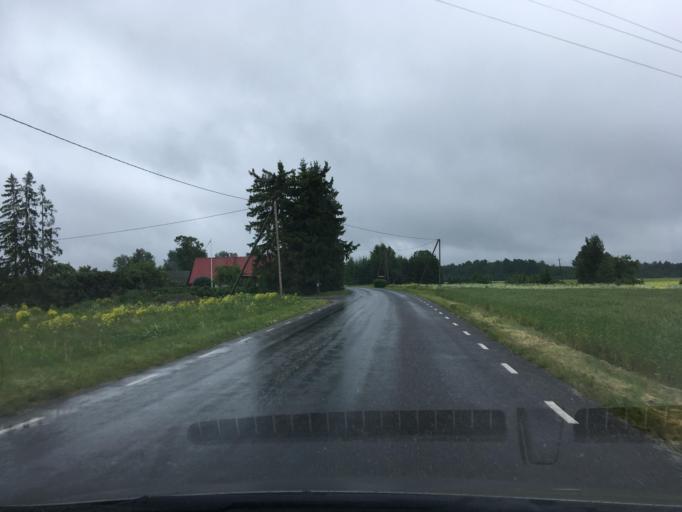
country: EE
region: Laeaene
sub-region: Lihula vald
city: Lihula
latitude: 58.6597
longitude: 23.7719
